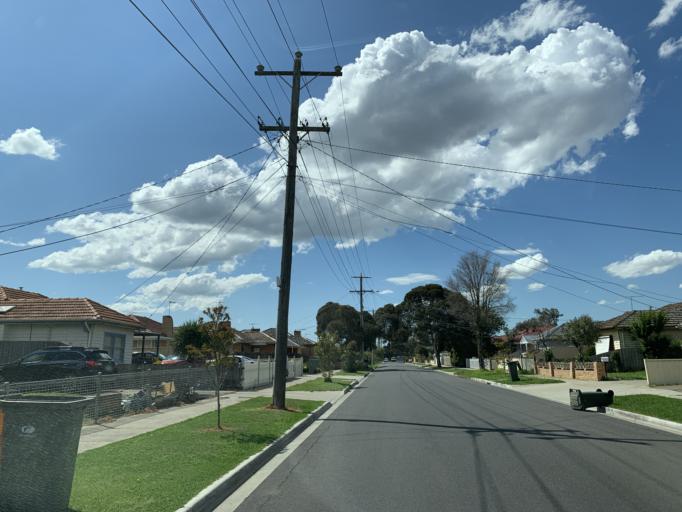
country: AU
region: Victoria
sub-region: Brimbank
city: Sunshine North
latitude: -37.7648
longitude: 144.8260
